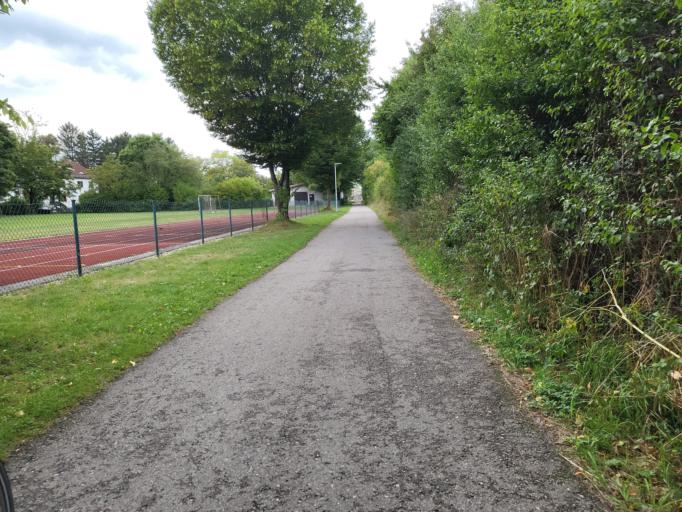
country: DE
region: Bavaria
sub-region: Upper Bavaria
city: Olching
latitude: 48.2120
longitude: 11.3203
